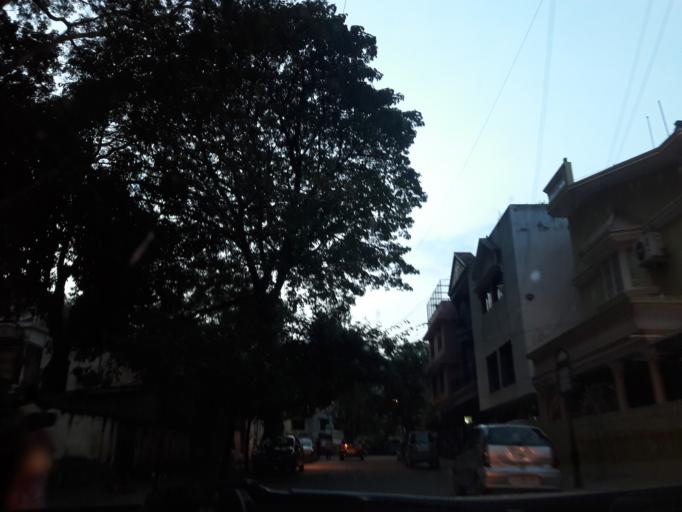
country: IN
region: Karnataka
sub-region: Bangalore Urban
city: Bangalore
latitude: 12.9454
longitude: 77.5793
